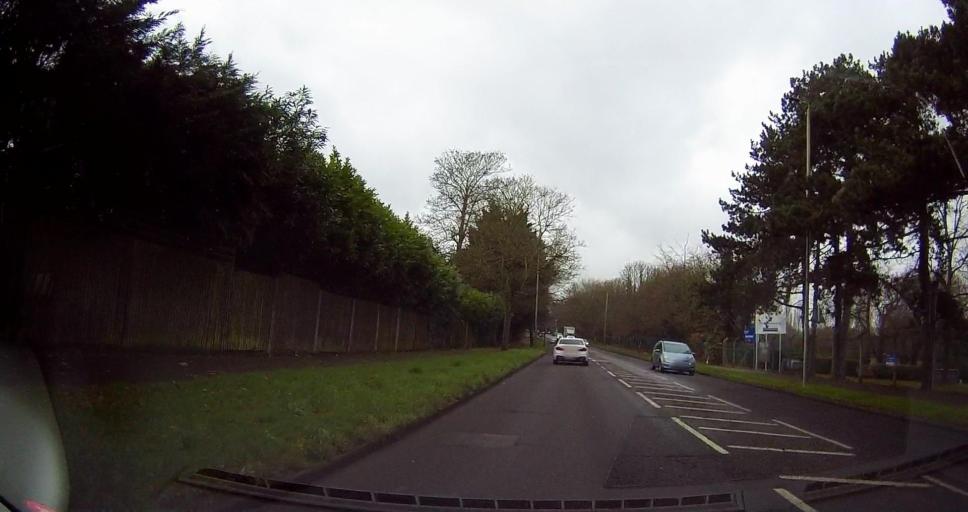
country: GB
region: England
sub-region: Greater London
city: Chislehurst
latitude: 51.4161
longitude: 0.0869
